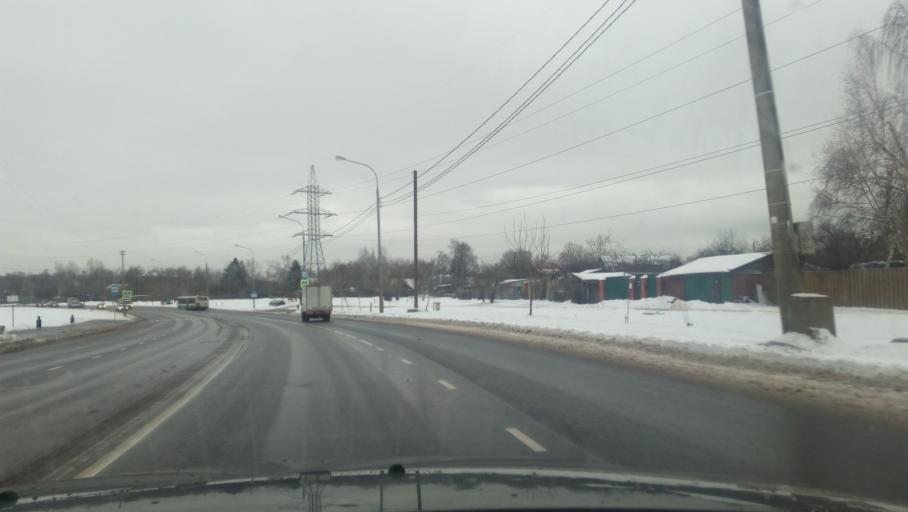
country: RU
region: Moscow
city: Zhulebino
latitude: 55.7234
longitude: 37.8592
